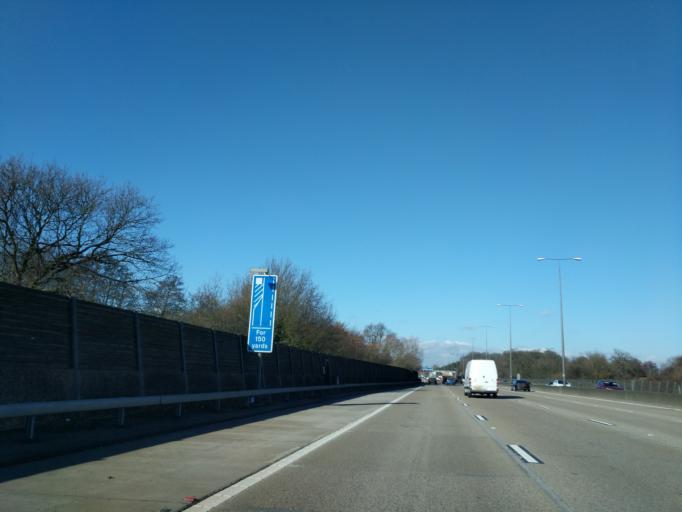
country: GB
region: England
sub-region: Surrey
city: Addlestone
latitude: 51.3570
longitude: -0.4944
